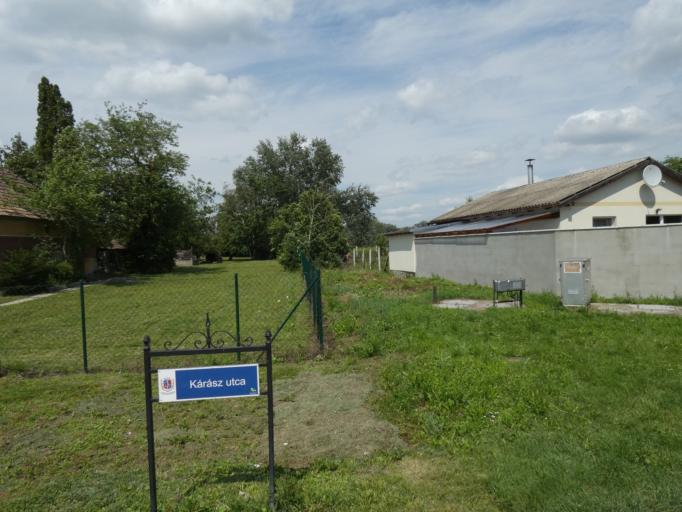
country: HU
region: Gyor-Moson-Sopron
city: Halaszi
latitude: 47.9509
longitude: 17.3476
